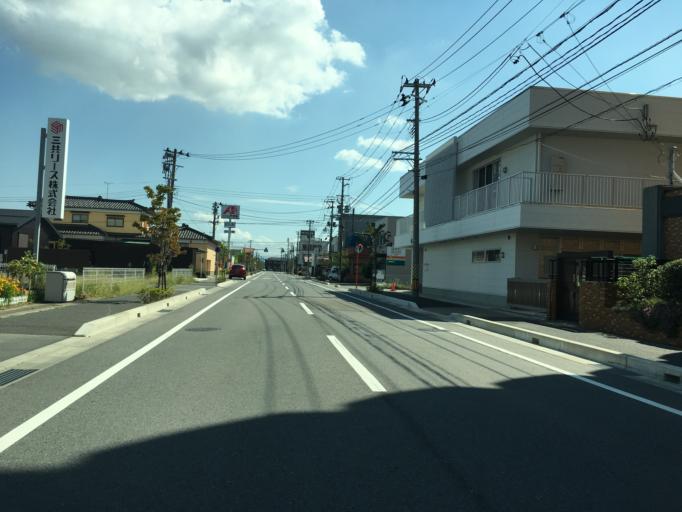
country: JP
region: Niigata
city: Kameda-honcho
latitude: 37.9116
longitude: 139.0754
